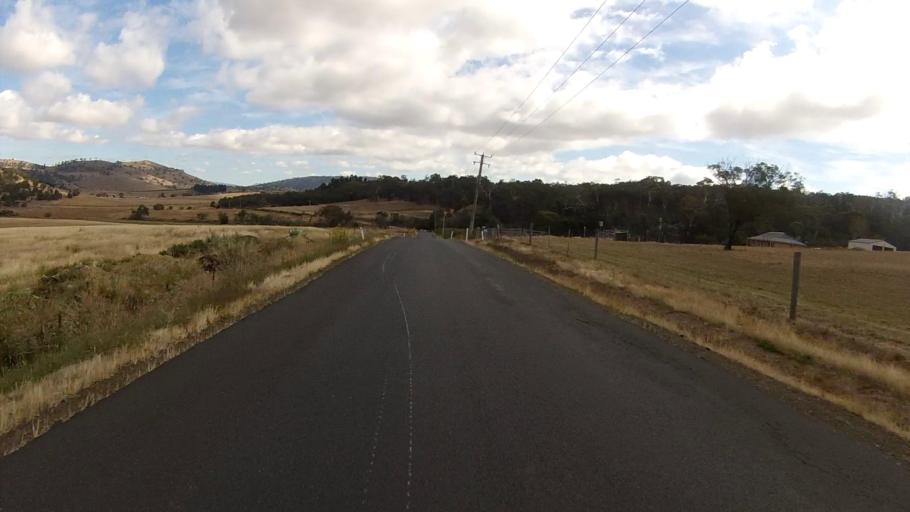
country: AU
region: Tasmania
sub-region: Brighton
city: Old Beach
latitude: -42.7556
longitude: 147.3050
